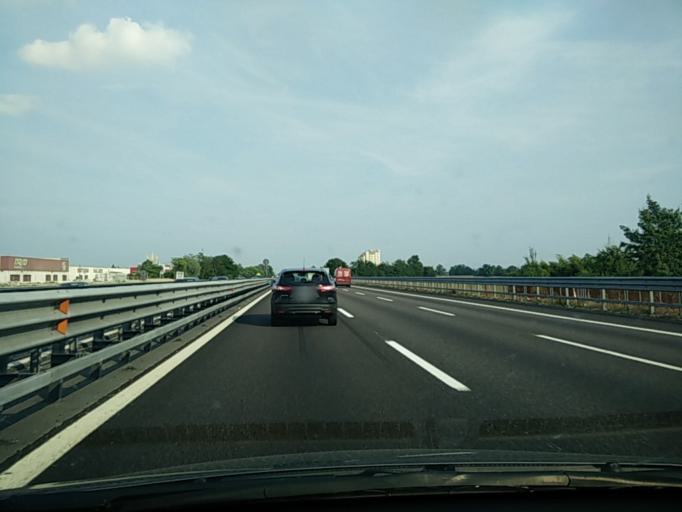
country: IT
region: Lombardy
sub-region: Citta metropolitana di Milano
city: Buccinasco
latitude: 45.4070
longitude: 9.1128
